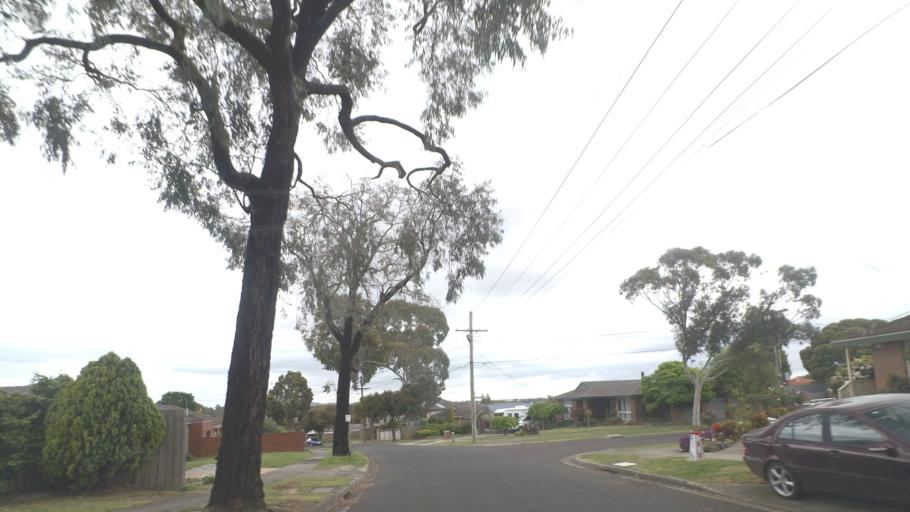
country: AU
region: Victoria
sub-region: Knox
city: Bayswater
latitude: -37.8521
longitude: 145.2523
